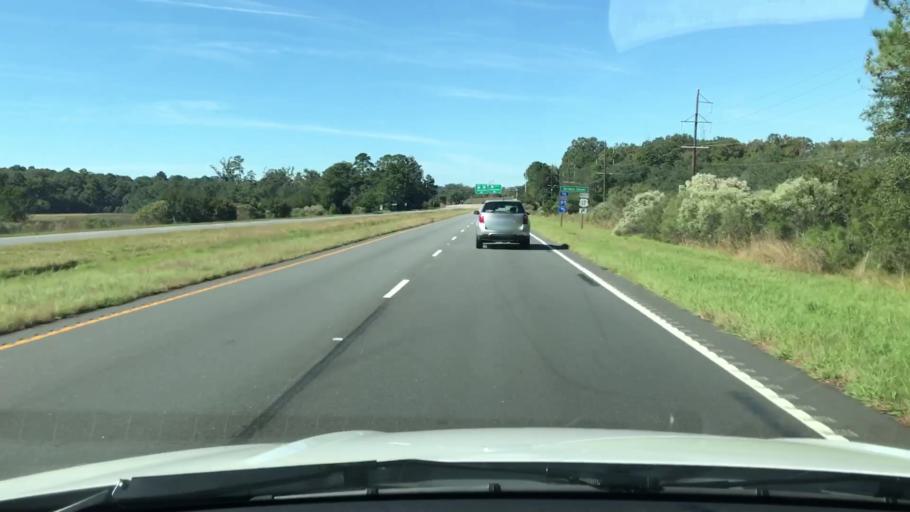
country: US
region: South Carolina
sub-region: Hampton County
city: Yemassee
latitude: 32.5964
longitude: -80.7546
